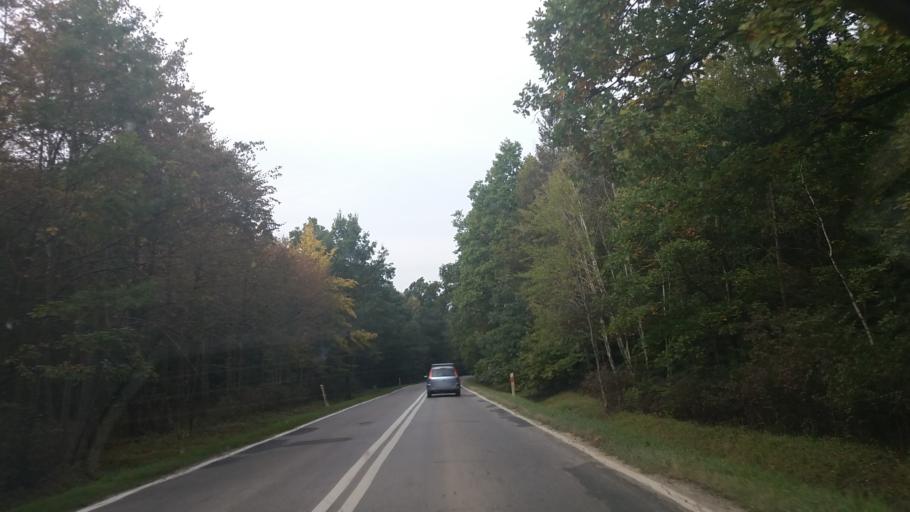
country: PL
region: Lesser Poland Voivodeship
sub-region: Powiat chrzanowski
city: Pogorzyce
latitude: 50.1183
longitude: 19.4389
